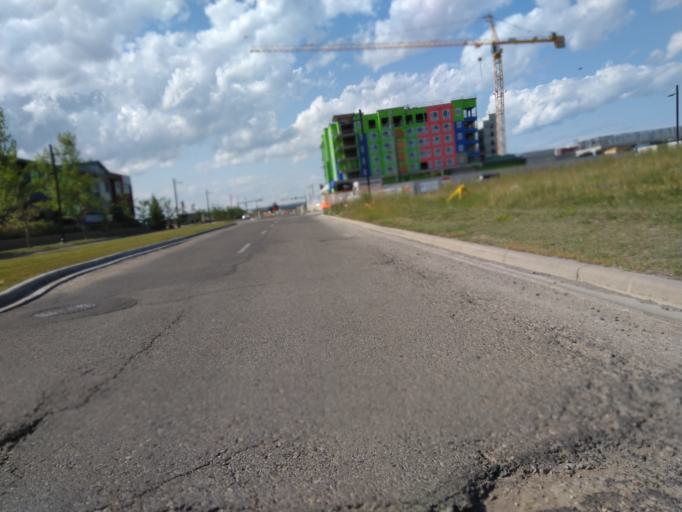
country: CA
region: Alberta
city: Calgary
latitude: 51.0759
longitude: -114.1461
